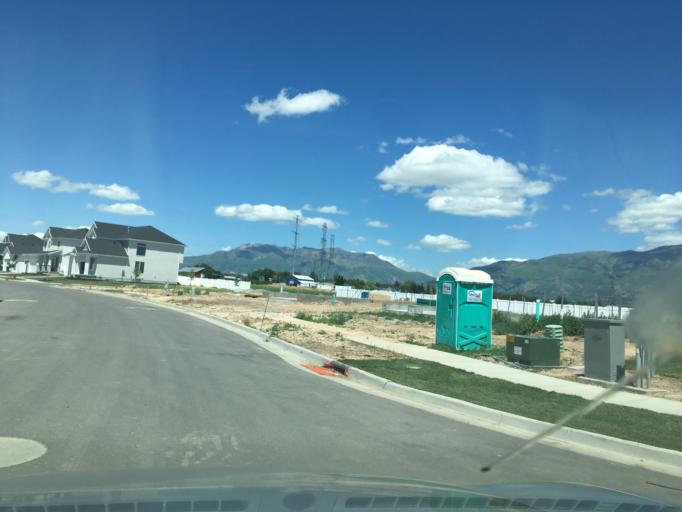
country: US
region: Utah
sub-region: Davis County
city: Layton
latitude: 41.0552
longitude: -112.0115
